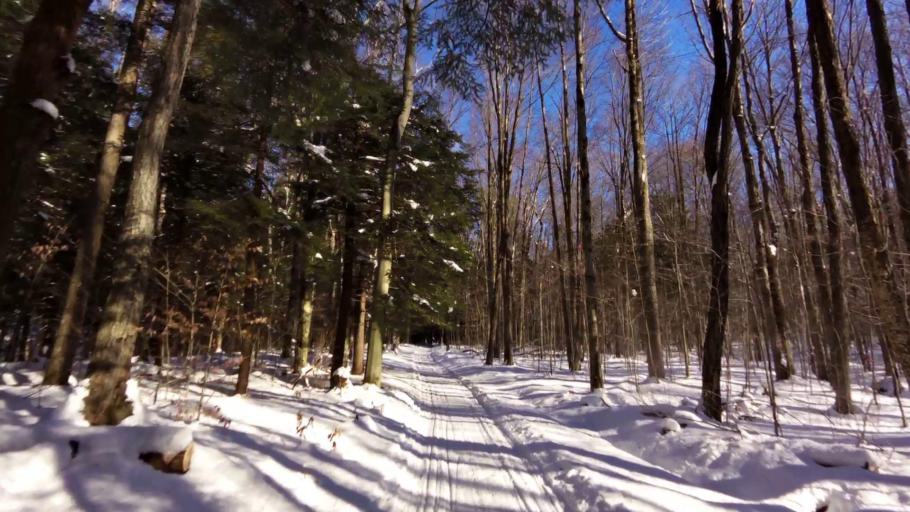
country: US
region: New York
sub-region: Cattaraugus County
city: Salamanca
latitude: 42.0747
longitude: -78.7009
